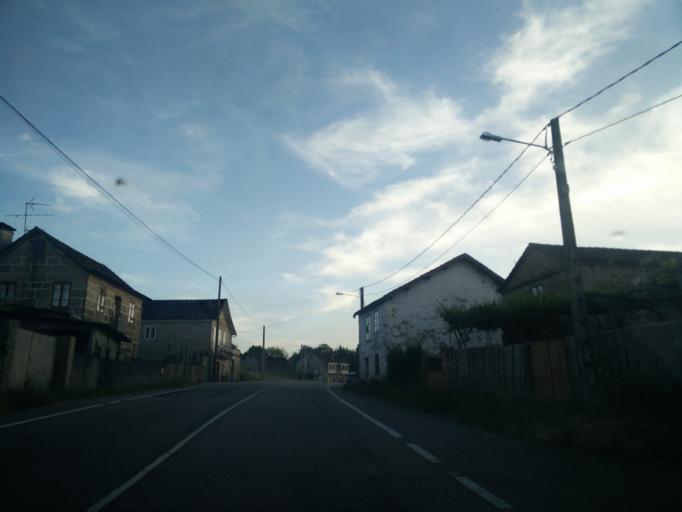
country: ES
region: Galicia
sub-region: Provincia de Pontevedra
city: Mondariz-Balneario
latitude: 42.2189
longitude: -8.4932
